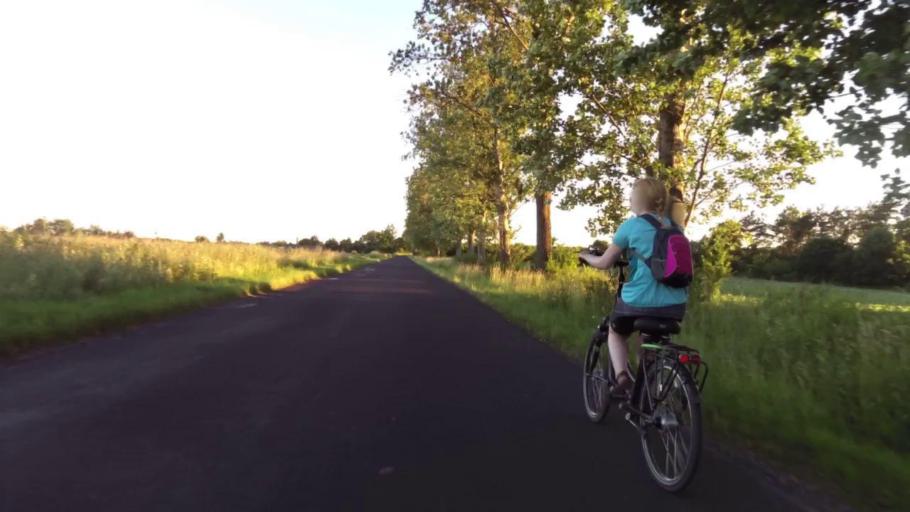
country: PL
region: West Pomeranian Voivodeship
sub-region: Powiat bialogardzki
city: Bialogard
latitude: 54.0352
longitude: 16.0441
